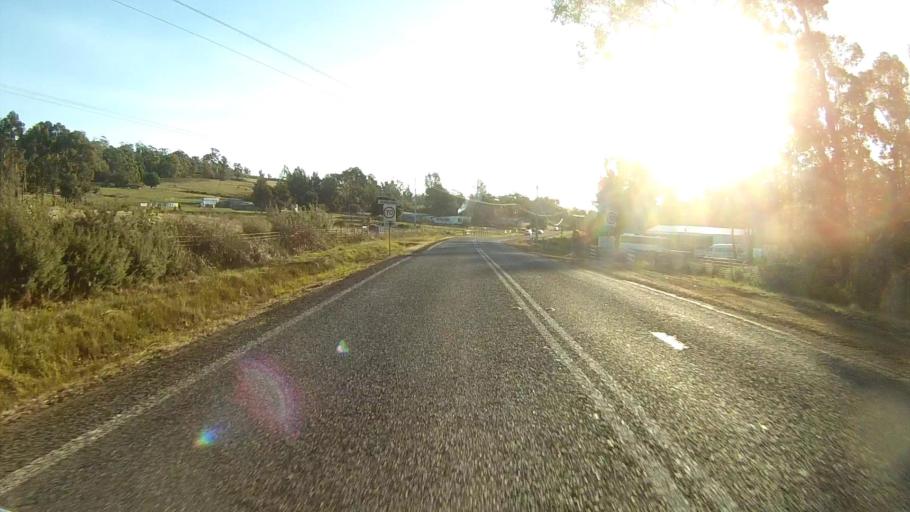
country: AU
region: Tasmania
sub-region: Sorell
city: Sorell
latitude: -42.9522
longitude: 147.8715
